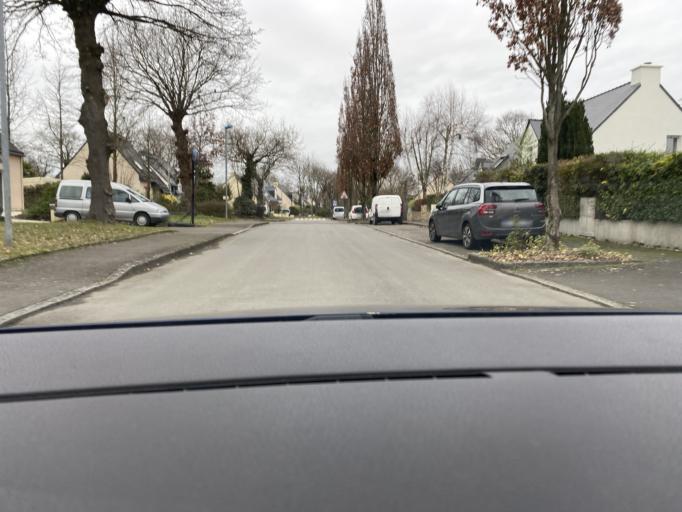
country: FR
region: Brittany
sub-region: Departement d'Ille-et-Vilaine
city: Melesse
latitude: 48.2220
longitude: -1.6928
